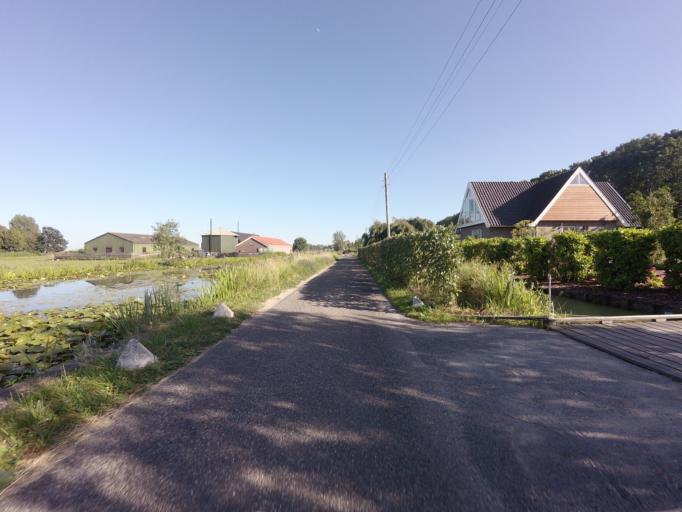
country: NL
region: South Holland
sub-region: Gemeente Vlist
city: Haastrecht
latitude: 52.0193
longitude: 4.7475
